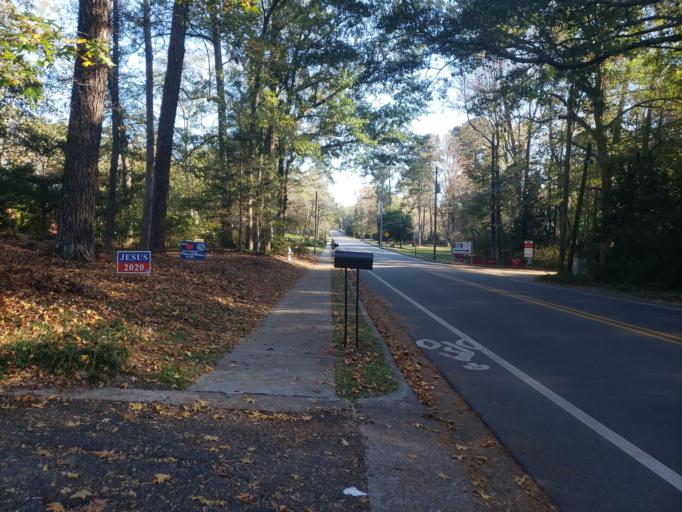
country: US
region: Alabama
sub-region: Lee County
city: Auburn
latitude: 32.5888
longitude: -85.4785
